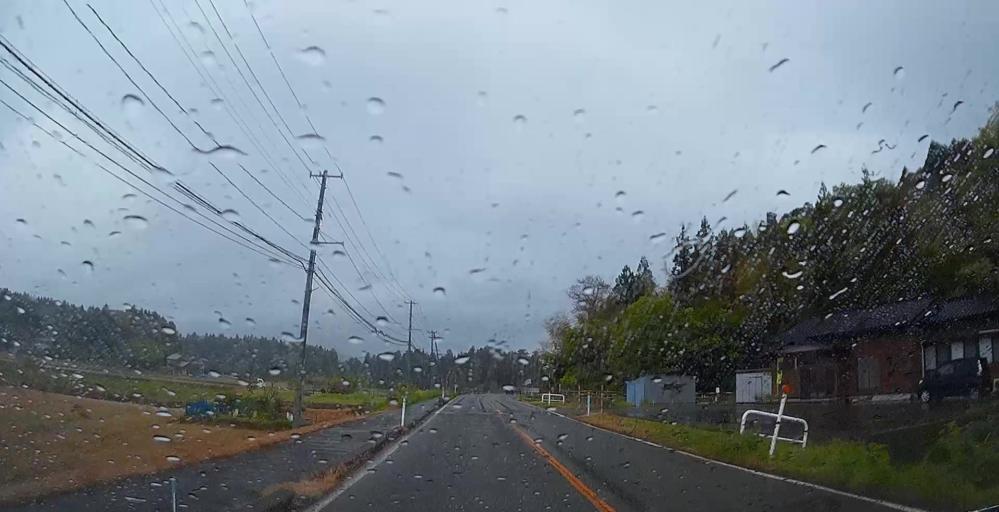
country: JP
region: Niigata
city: Kashiwazaki
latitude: 37.4463
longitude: 138.6449
